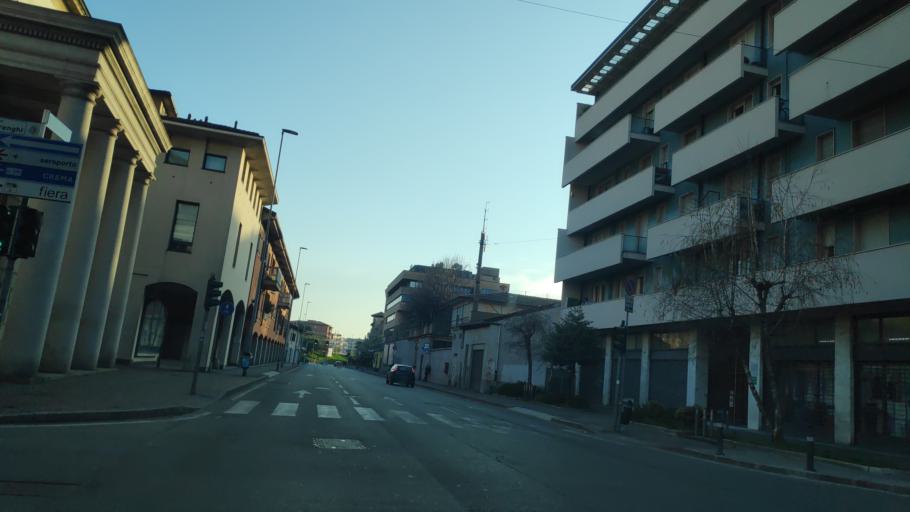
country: IT
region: Lombardy
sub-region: Provincia di Bergamo
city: Bergamo
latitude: 45.6895
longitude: 9.6692
